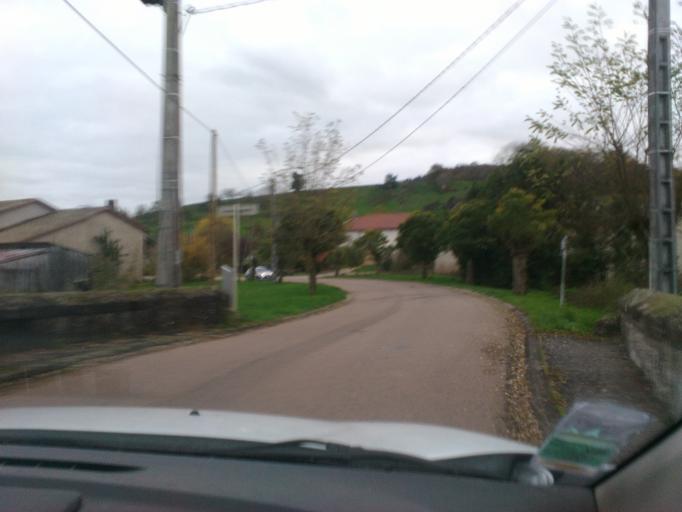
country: FR
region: Lorraine
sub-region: Departement des Vosges
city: Vincey
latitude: 48.2655
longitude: 6.2715
